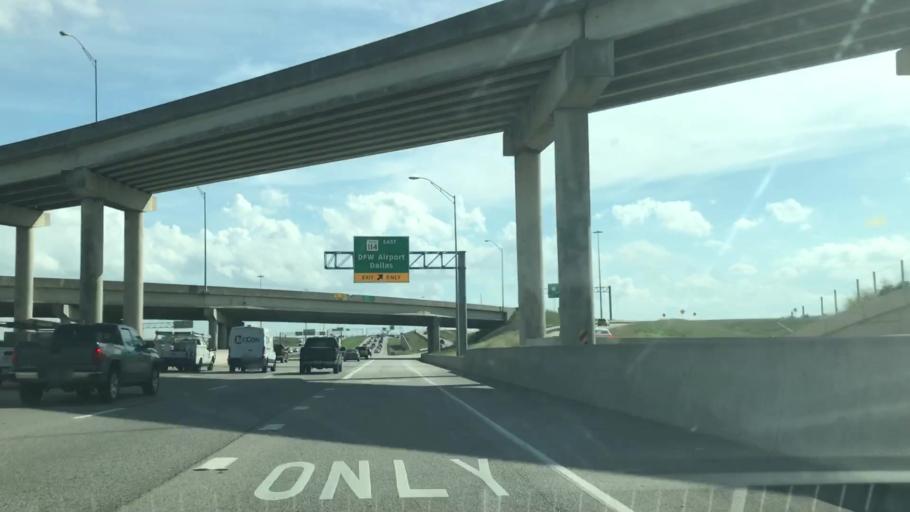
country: US
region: Texas
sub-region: Dallas County
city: Coppell
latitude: 32.9505
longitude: -97.0404
